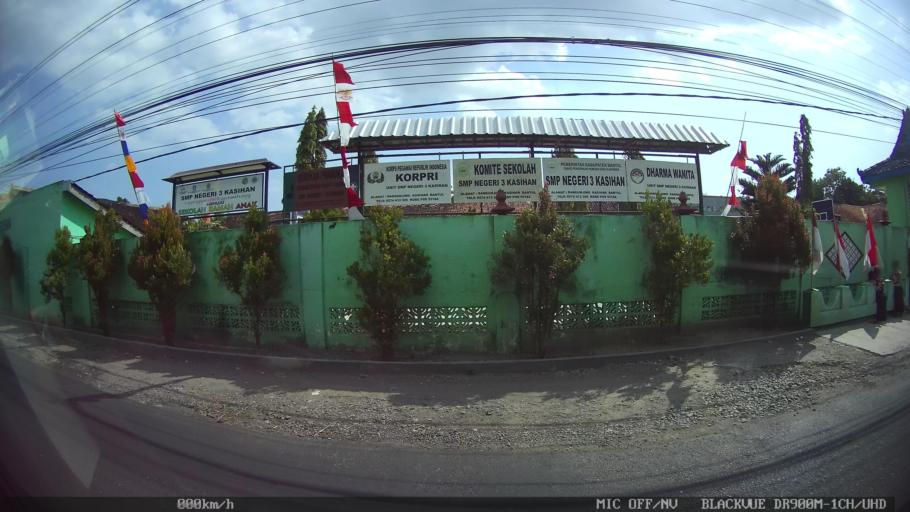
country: ID
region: Daerah Istimewa Yogyakarta
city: Kasihan
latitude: -7.8398
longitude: 110.3131
